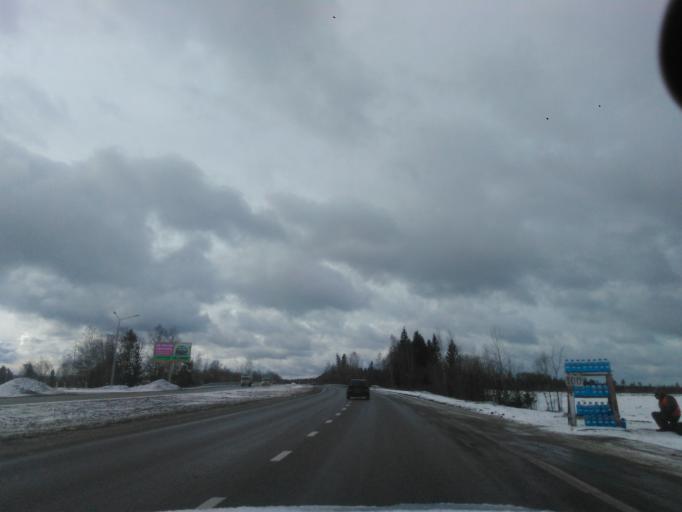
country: RU
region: Moscow
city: Zelenograd
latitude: 55.9477
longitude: 37.1752
